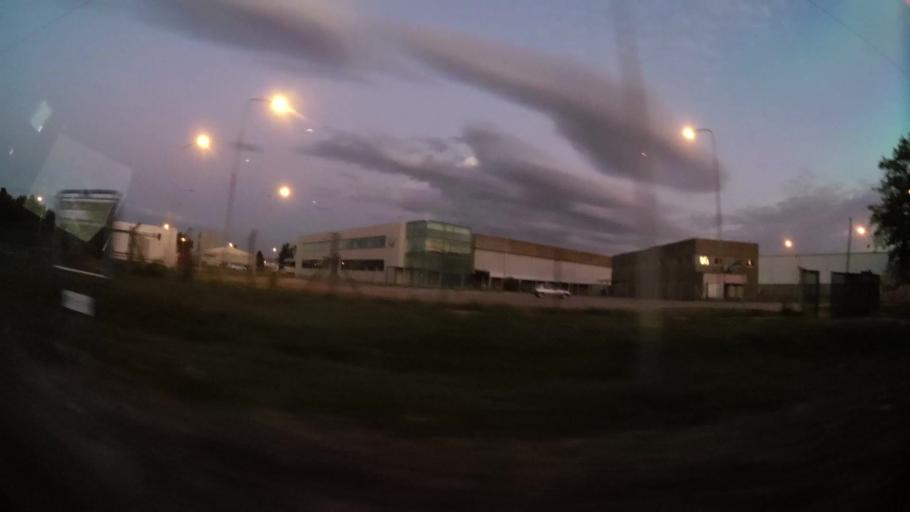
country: AR
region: Buenos Aires
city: Santa Catalina - Dique Lujan
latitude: -34.4599
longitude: -58.7437
